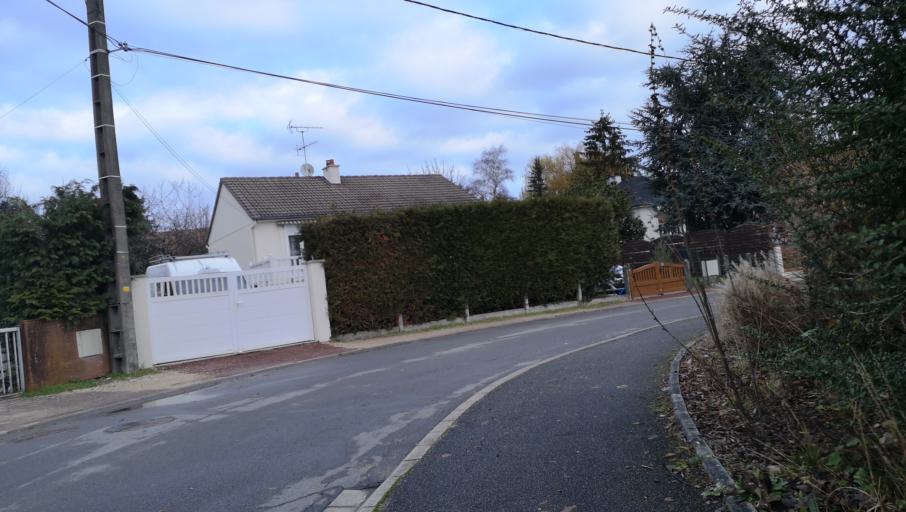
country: FR
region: Centre
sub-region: Departement du Loiret
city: Boigny-sur-Bionne
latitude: 47.9214
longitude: 2.0057
